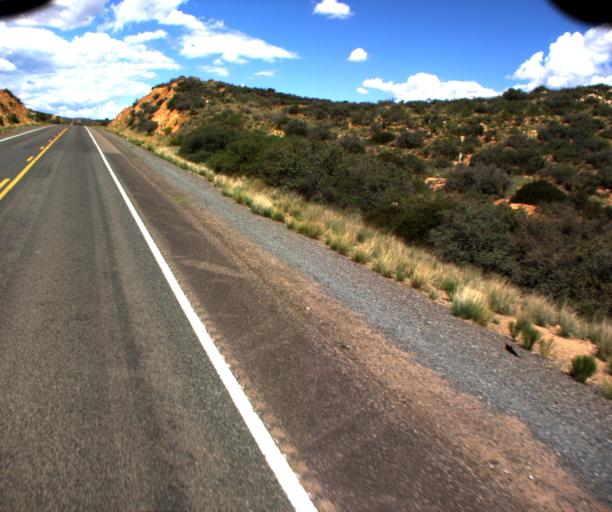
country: US
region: Arizona
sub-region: Yavapai County
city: Dewey-Humboldt
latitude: 34.5267
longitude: -112.0921
